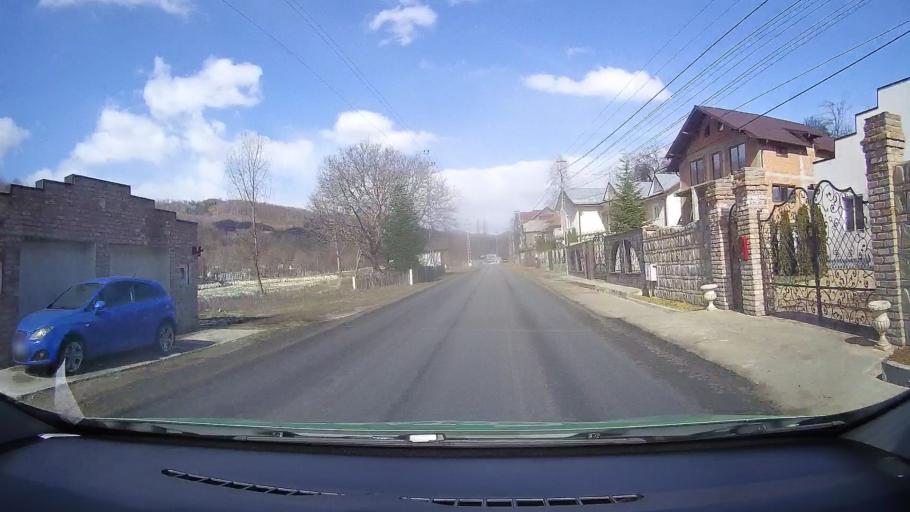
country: RO
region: Dambovita
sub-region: Comuna Runcu
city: Badeni
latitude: 45.1520
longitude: 25.4011
